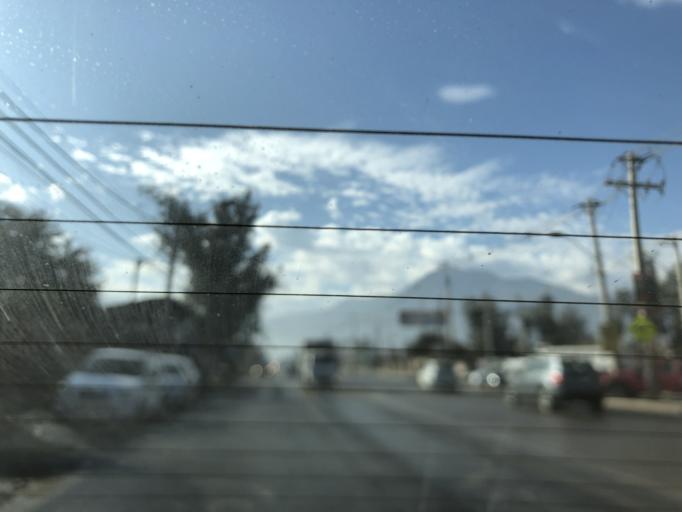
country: CL
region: Santiago Metropolitan
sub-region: Provincia de Cordillera
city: Puente Alto
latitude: -33.5982
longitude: -70.5217
